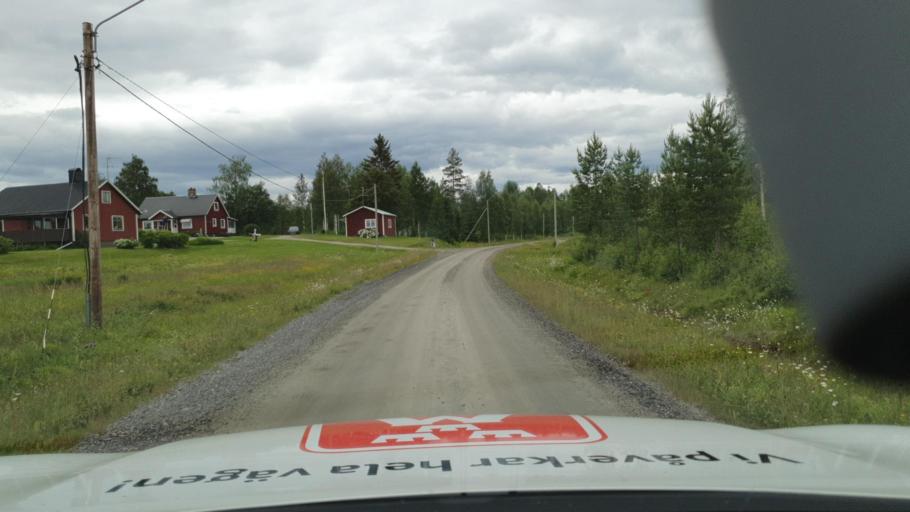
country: SE
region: Vaesterbotten
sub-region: Bjurholms Kommun
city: Bjurholm
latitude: 63.7253
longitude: 19.3102
